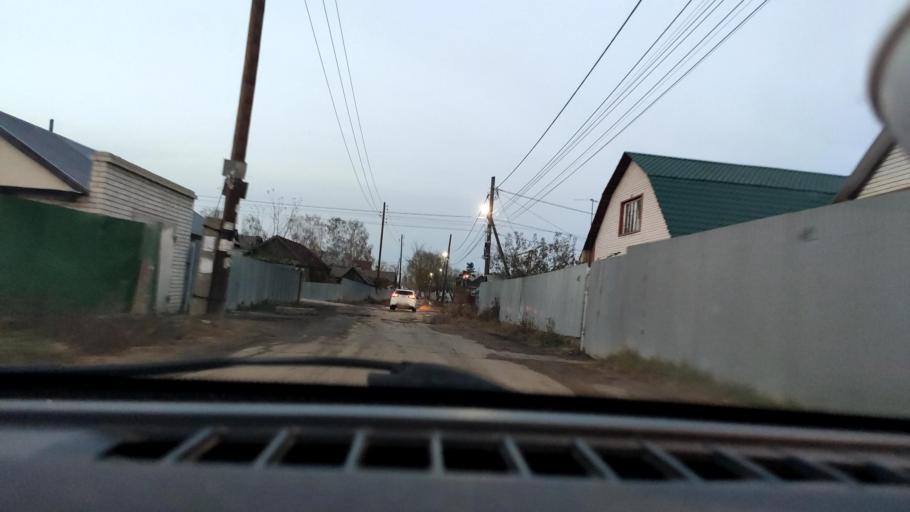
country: RU
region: Samara
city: Samara
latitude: 53.1404
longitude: 50.0965
